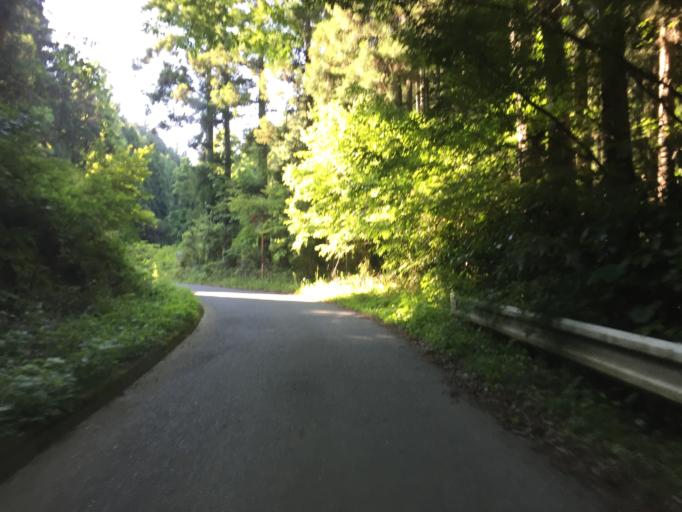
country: JP
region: Ibaraki
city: Kitaibaraki
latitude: 36.8691
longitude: 140.7030
